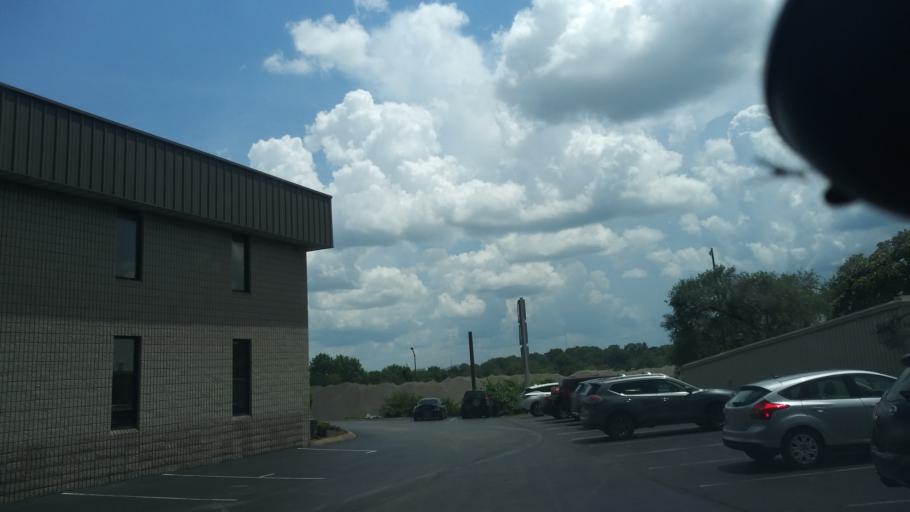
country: US
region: Tennessee
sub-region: Davidson County
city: Oak Hill
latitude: 36.1224
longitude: -86.7631
